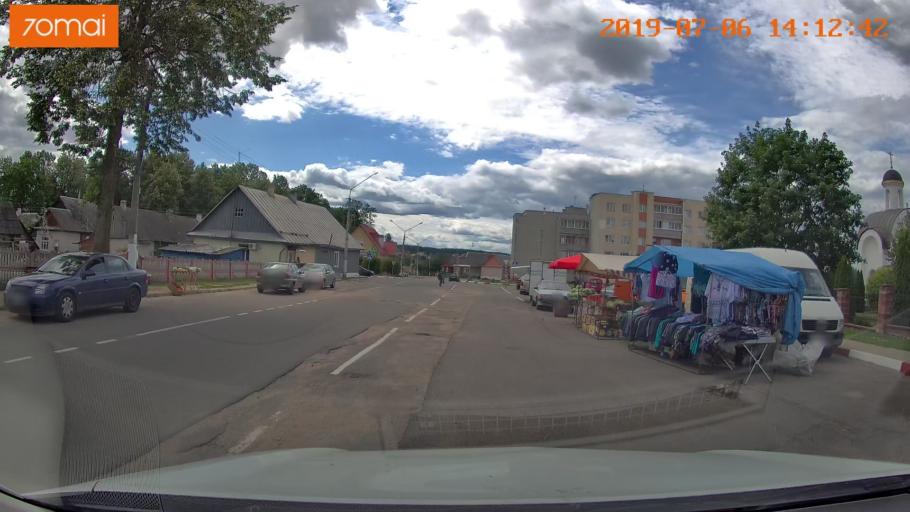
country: BY
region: Minsk
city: Ivyanyets
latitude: 53.8897
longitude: 26.7418
